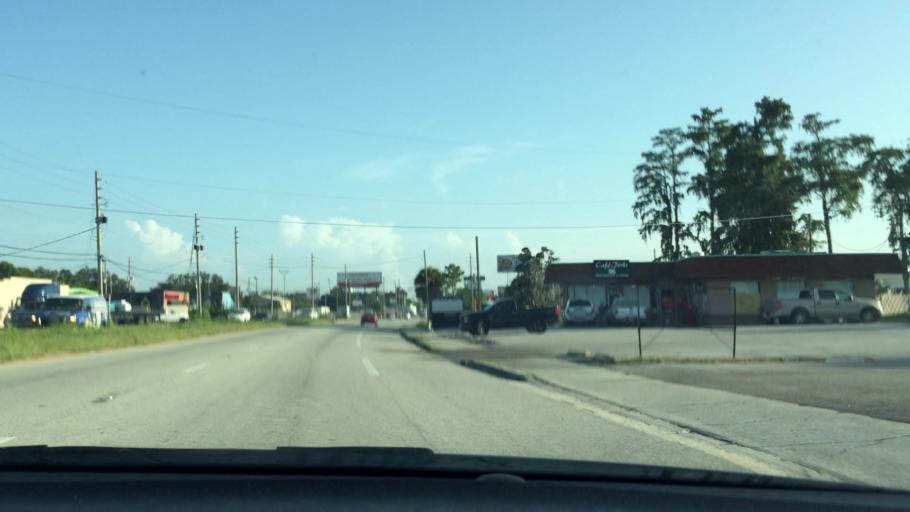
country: US
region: Florida
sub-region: Orange County
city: Fairview Shores
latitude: 28.5748
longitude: -81.4068
